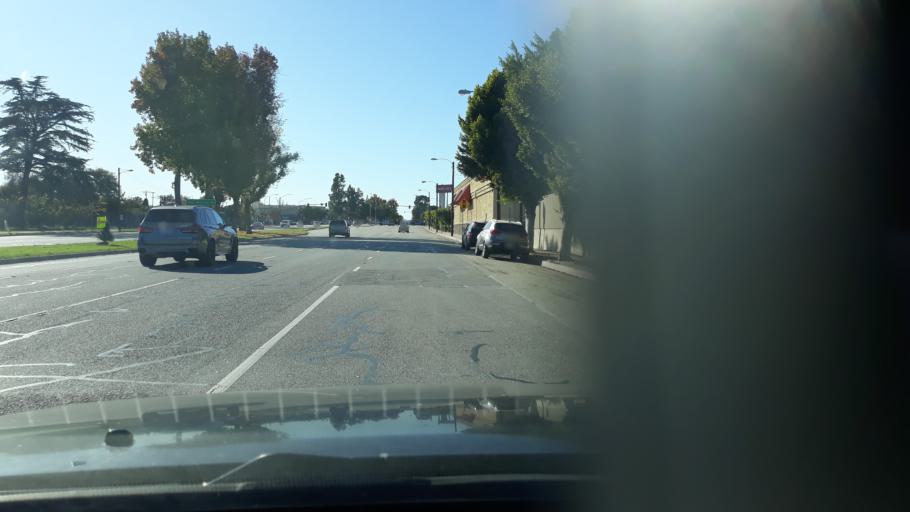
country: US
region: California
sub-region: Los Angeles County
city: East Pasadena
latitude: 34.1279
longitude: -118.0884
